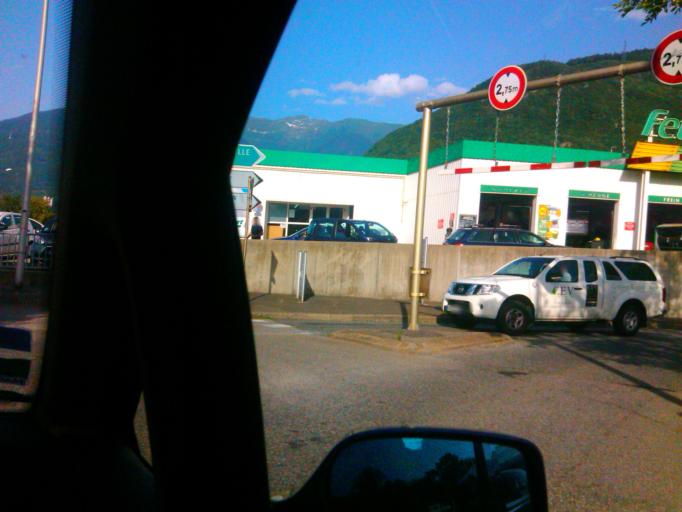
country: FR
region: Rhone-Alpes
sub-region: Departement de la Savoie
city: Grignon
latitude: 45.6557
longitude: 6.3659
